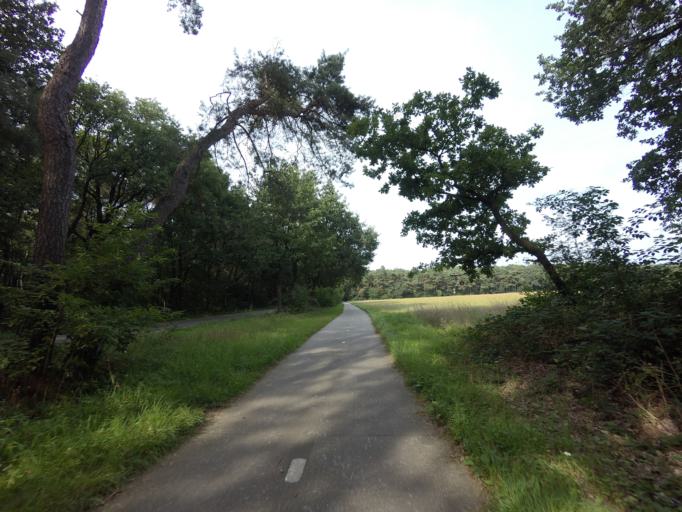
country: DE
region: Lower Saxony
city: Getelo
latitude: 52.4539
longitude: 6.8326
